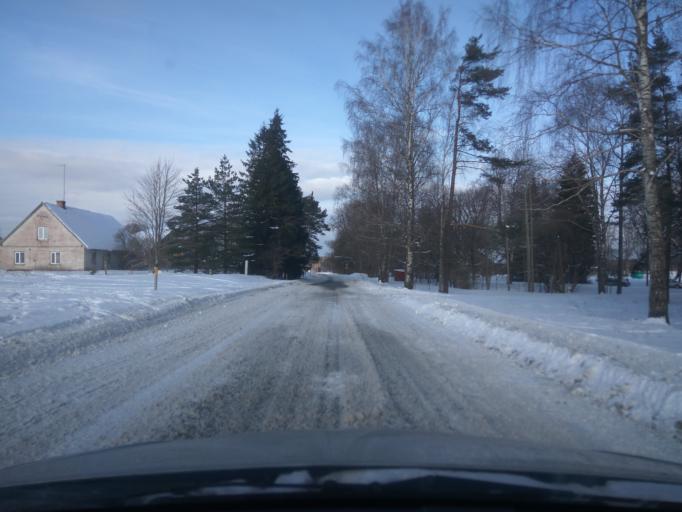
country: LV
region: Ventspils Rajons
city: Piltene
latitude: 57.4005
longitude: 21.8666
